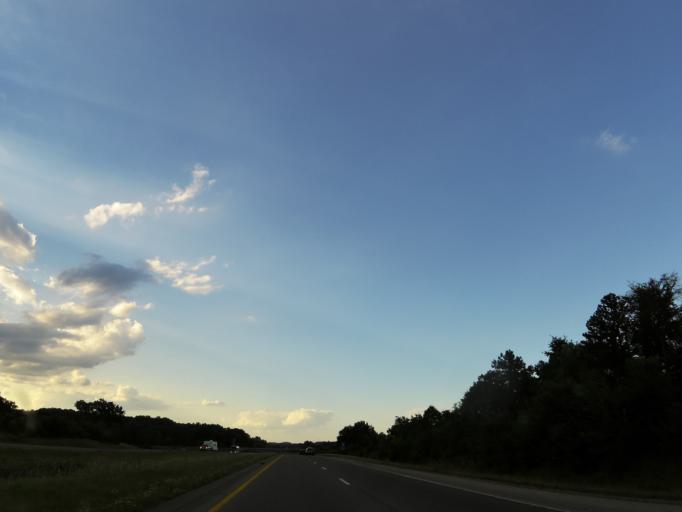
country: US
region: Tennessee
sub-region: Maury County
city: Spring Hill
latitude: 35.7345
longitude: -86.8742
